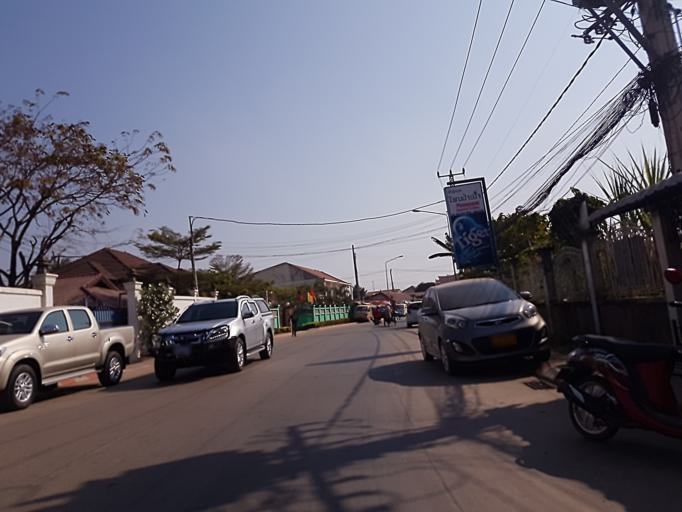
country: LA
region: Vientiane
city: Vientiane
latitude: 17.9499
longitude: 102.6403
